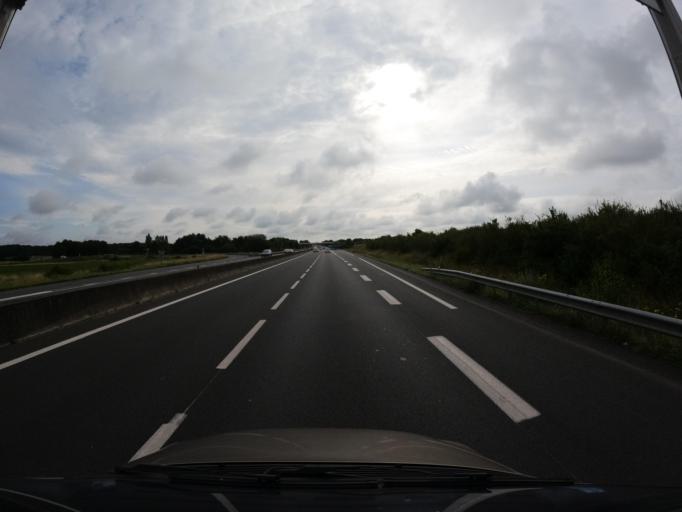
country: FR
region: Centre
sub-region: Departement d'Indre-et-Loire
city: Savonnieres
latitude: 47.3019
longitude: 0.5453
